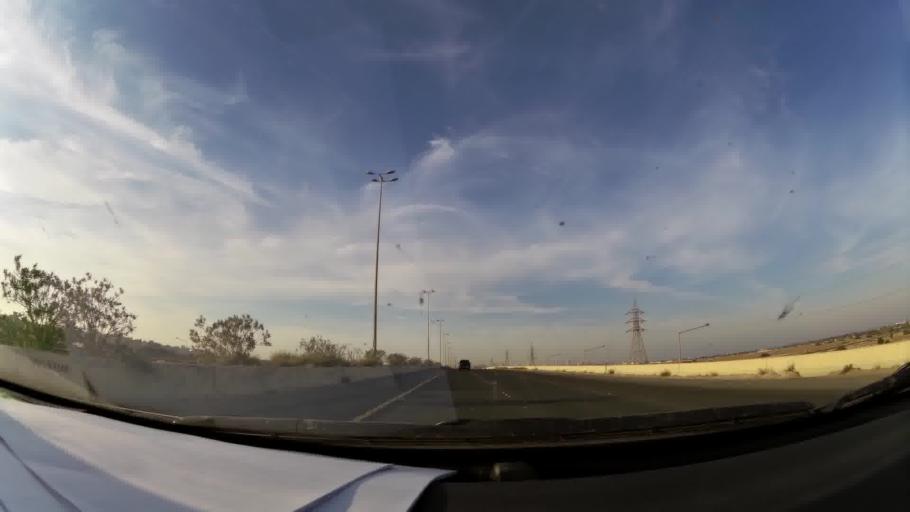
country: KW
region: Al Ahmadi
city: Al Fahahil
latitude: 28.9650
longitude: 48.1653
